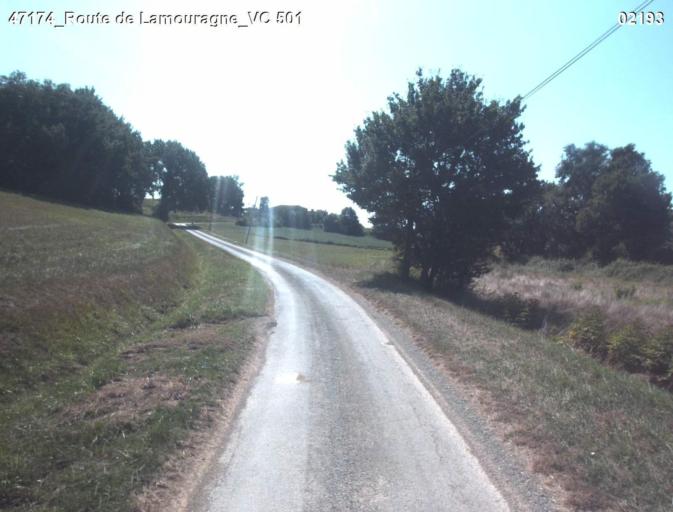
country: FR
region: Midi-Pyrenees
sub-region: Departement du Gers
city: Condom
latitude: 44.0296
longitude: 0.3945
